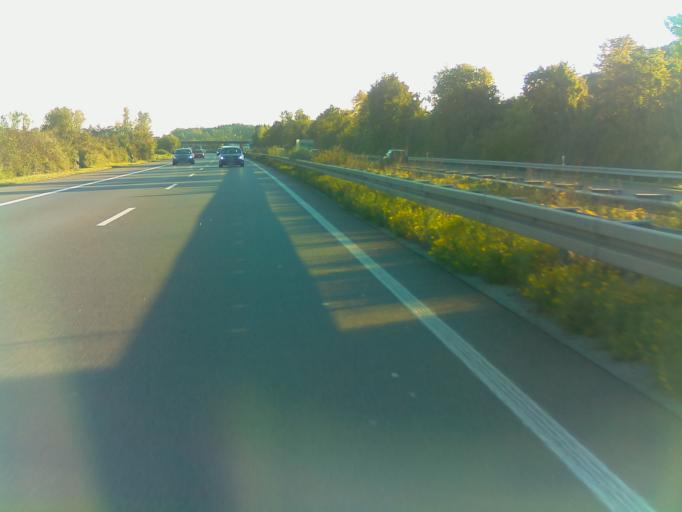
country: DE
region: Hesse
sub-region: Regierungsbezirk Darmstadt
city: Alsbach-Hahnlein
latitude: 49.7548
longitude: 8.5945
